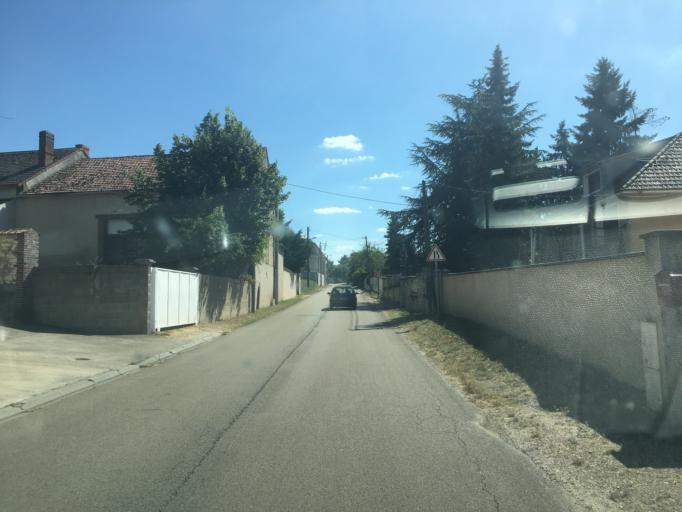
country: FR
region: Bourgogne
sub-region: Departement de l'Yonne
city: Fleury-la-Vallee
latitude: 47.8635
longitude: 3.4466
